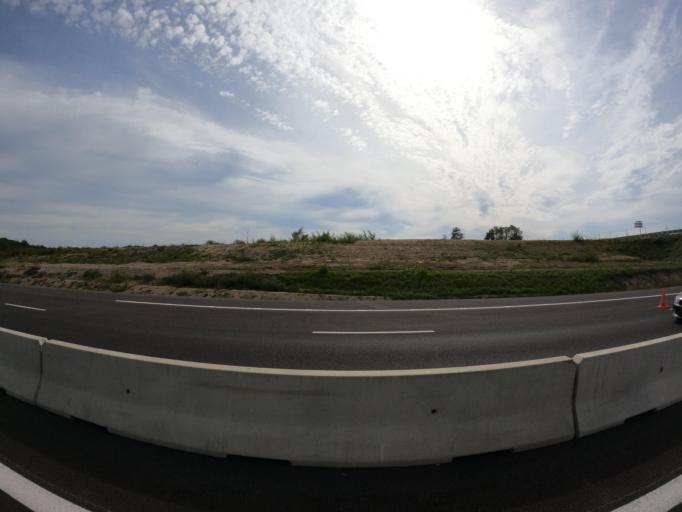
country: FR
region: Auvergne
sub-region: Departement de l'Allier
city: Lusigny
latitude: 46.5254
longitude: 3.4945
